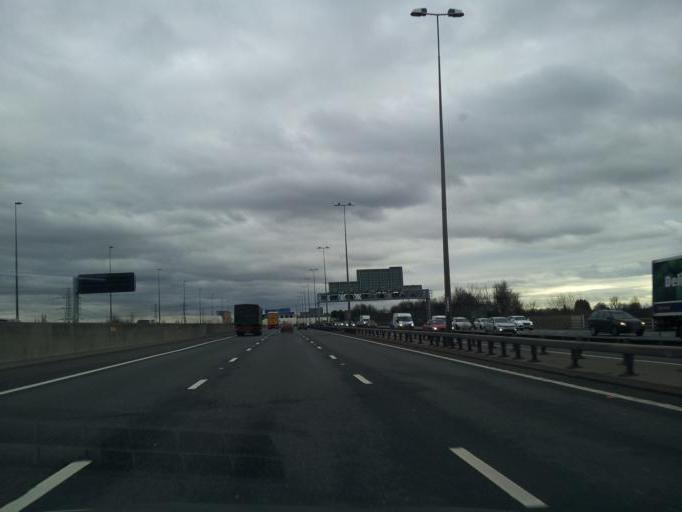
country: GB
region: England
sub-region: Warwickshire
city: Water Orton
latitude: 52.5219
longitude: -1.7274
